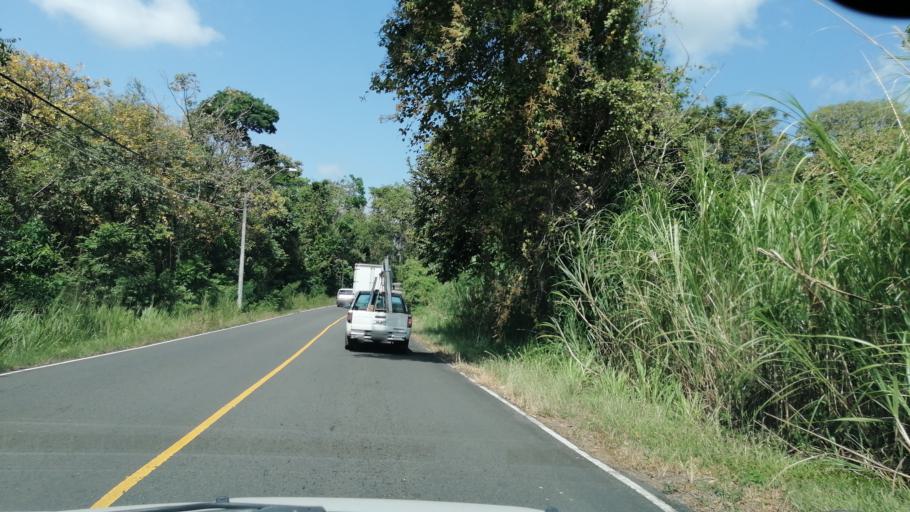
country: PA
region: Panama
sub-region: Distrito de Panama
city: Ancon
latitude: 8.9294
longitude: -79.5735
